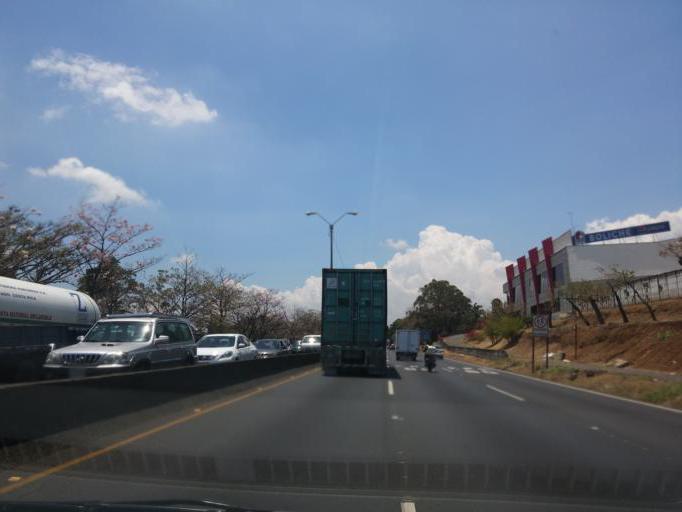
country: CR
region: Heredia
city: La Asuncion
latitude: 9.9774
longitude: -84.1558
